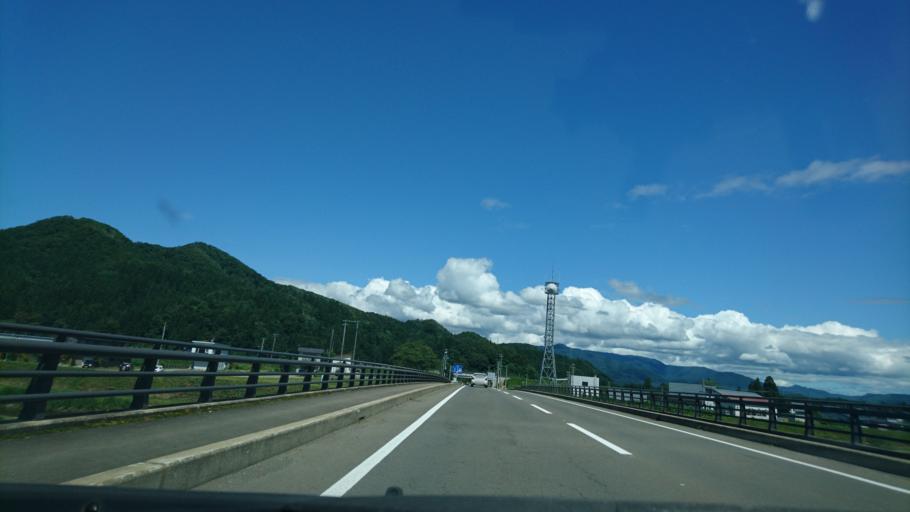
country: JP
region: Akita
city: Kakunodatemachi
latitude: 39.6058
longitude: 140.5584
